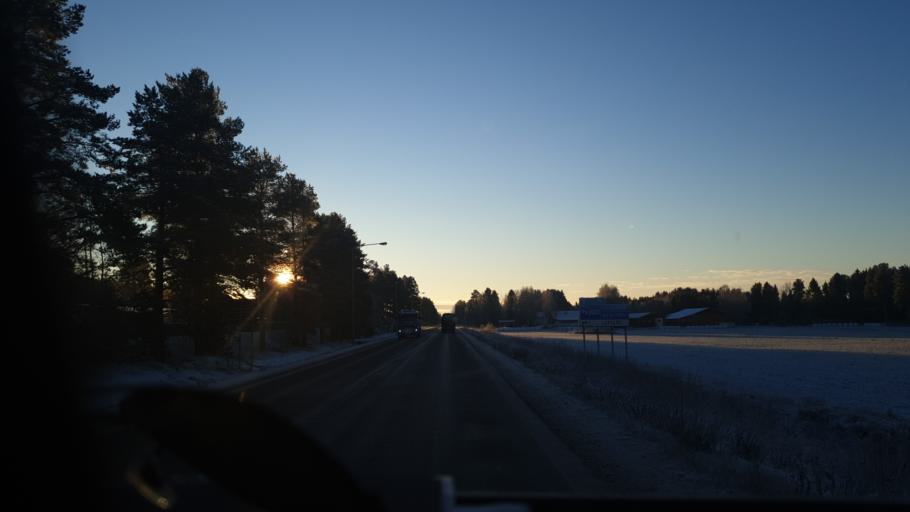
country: FI
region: Northern Ostrobothnia
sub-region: Ylivieska
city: Kalajoki
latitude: 64.2813
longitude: 23.9485
